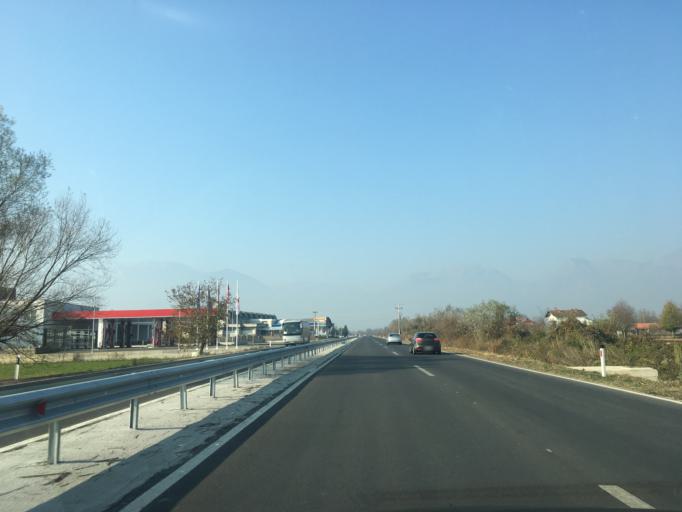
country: XK
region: Pec
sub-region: Komuna e Pejes
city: Dubova (Driloni)
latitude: 42.6589
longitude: 20.3767
